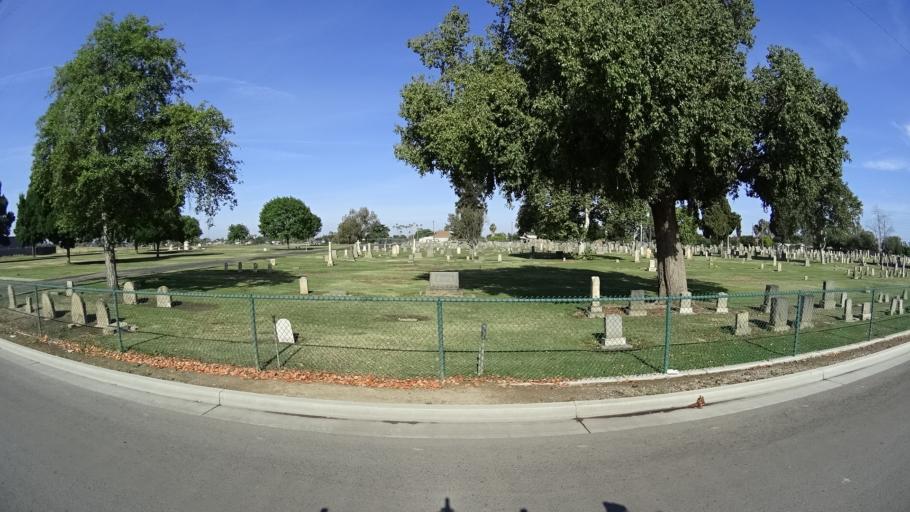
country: US
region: California
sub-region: Kings County
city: Hanford
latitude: 36.3210
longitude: -119.6370
